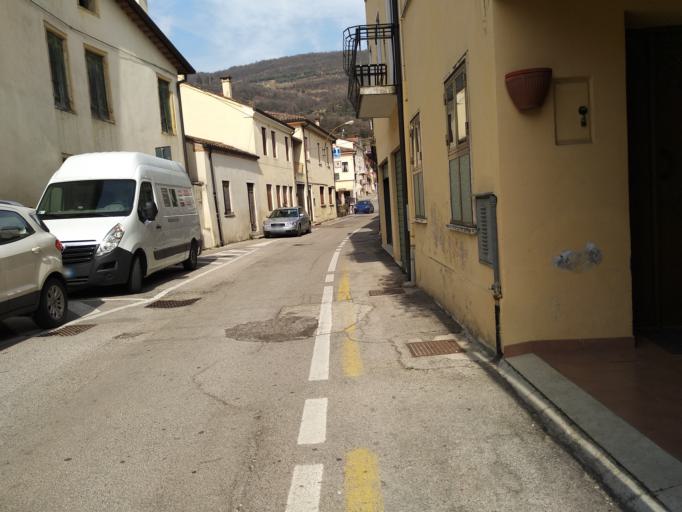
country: IT
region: Veneto
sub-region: Provincia di Vicenza
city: Barbarano Vicentino
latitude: 45.4092
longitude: 11.5395
